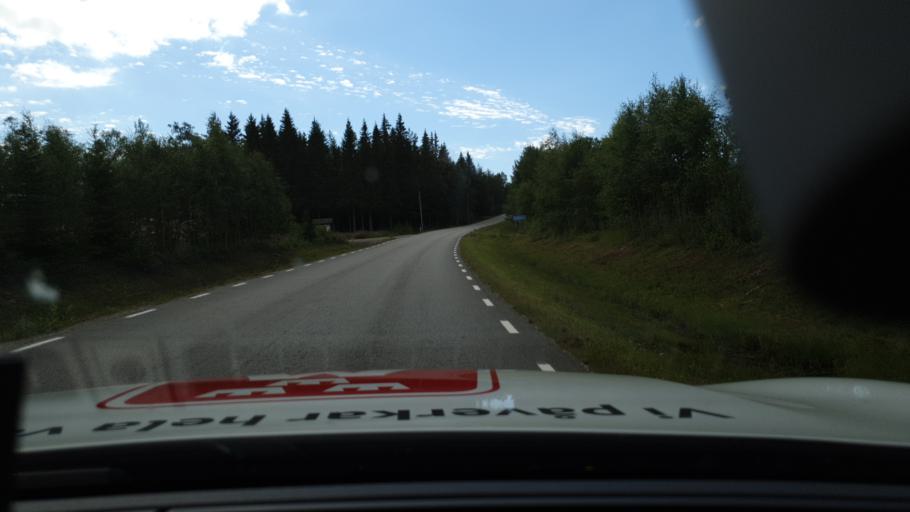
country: SE
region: Norrbotten
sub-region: Kalix Kommun
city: Toere
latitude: 65.8513
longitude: 22.6796
